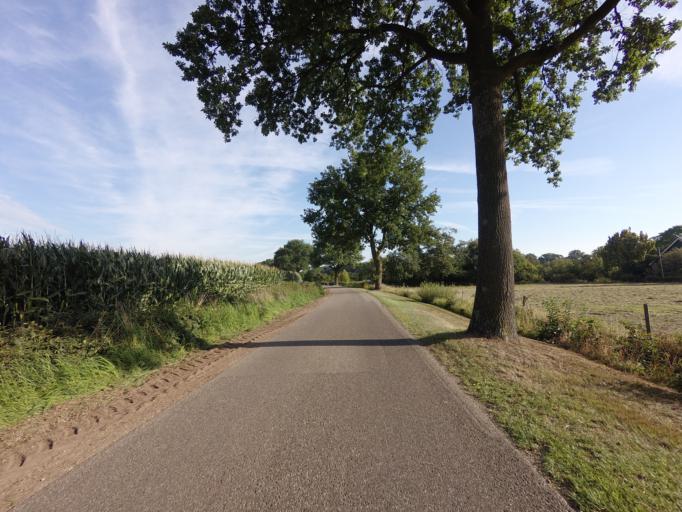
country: NL
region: Gelderland
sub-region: Oude IJsselstreek
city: Wisch
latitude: 51.9122
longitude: 6.4238
